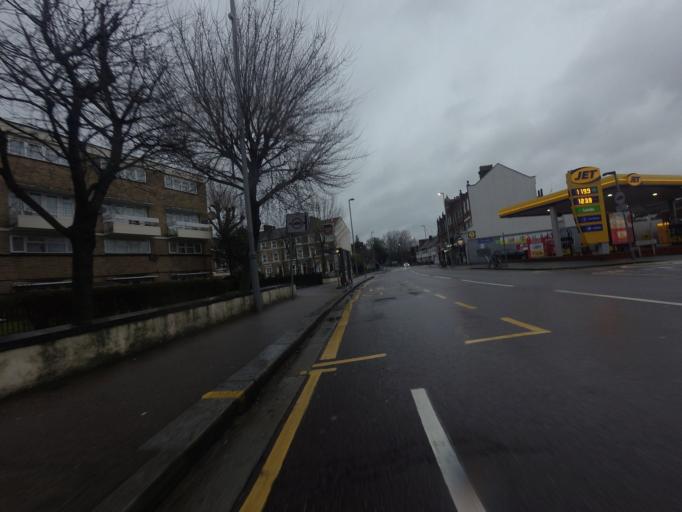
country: GB
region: England
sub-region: Greater London
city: Walthamstow
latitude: 51.5648
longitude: -0.0111
